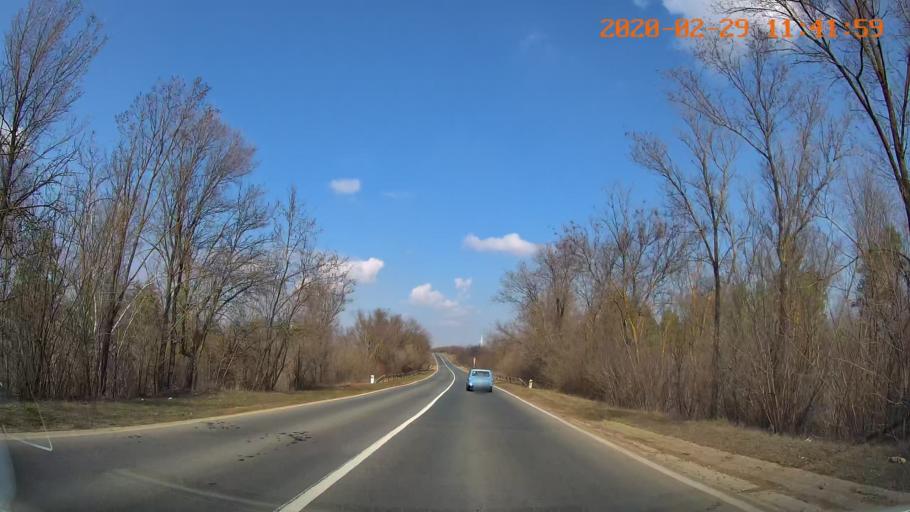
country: MD
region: Rezina
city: Saharna
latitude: 47.6784
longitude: 29.0147
